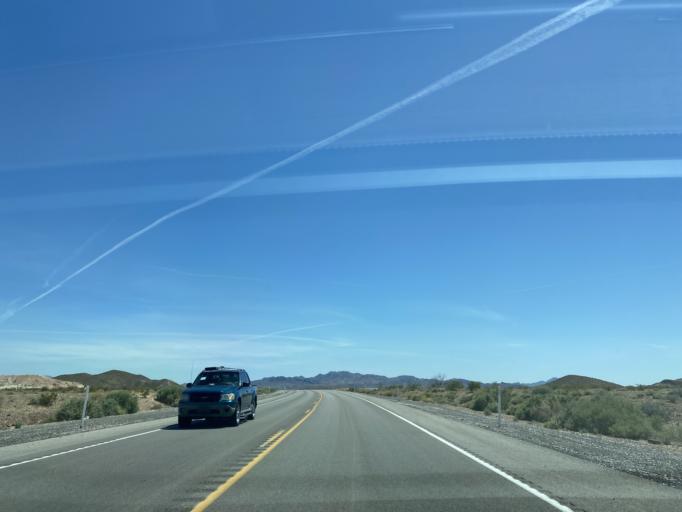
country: US
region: Nevada
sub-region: Clark County
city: Nellis Air Force Base
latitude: 36.1824
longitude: -114.9176
